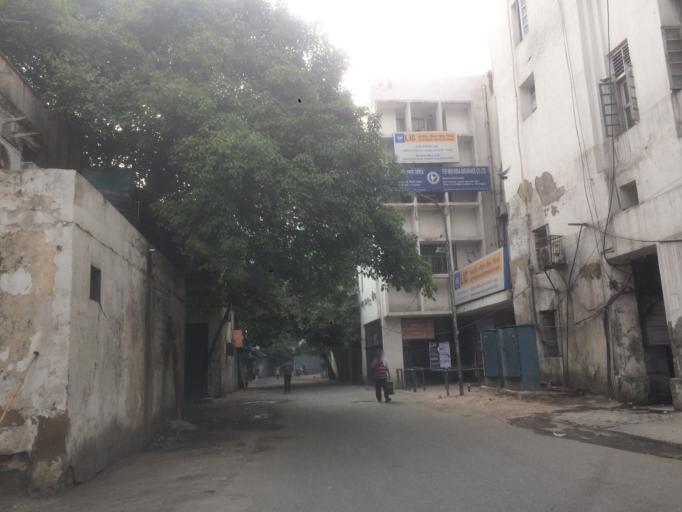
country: IN
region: NCT
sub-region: New Delhi
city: New Delhi
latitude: 28.6289
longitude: 77.2198
